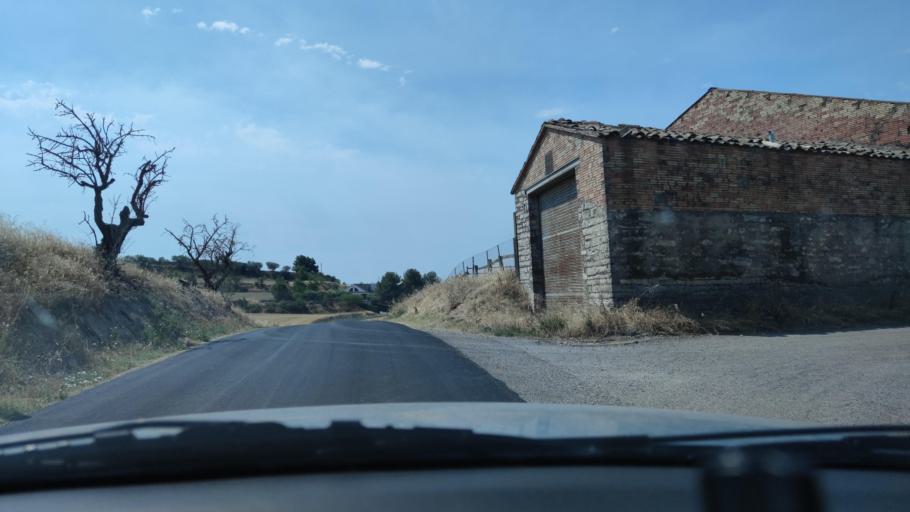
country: ES
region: Catalonia
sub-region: Provincia de Lleida
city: Ivorra
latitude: 41.7673
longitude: 1.3260
